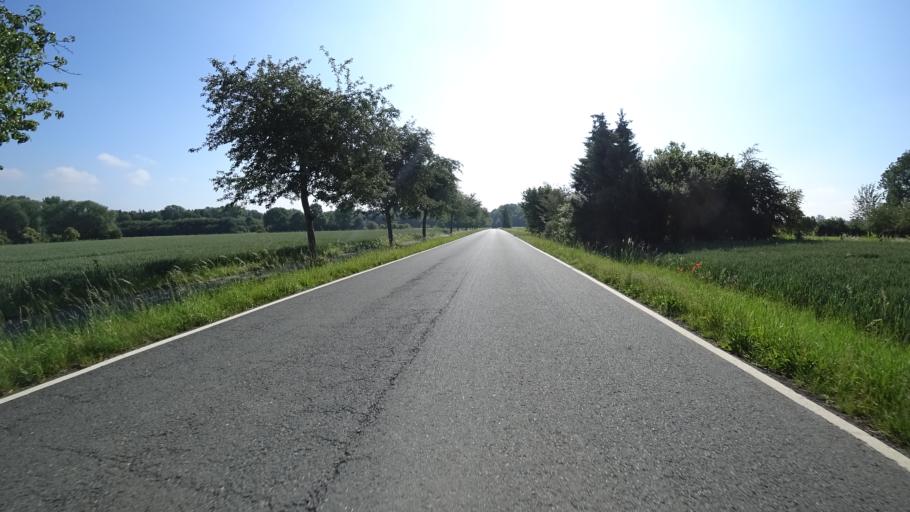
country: DE
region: North Rhine-Westphalia
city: Erwitte
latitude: 51.6323
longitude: 8.3794
